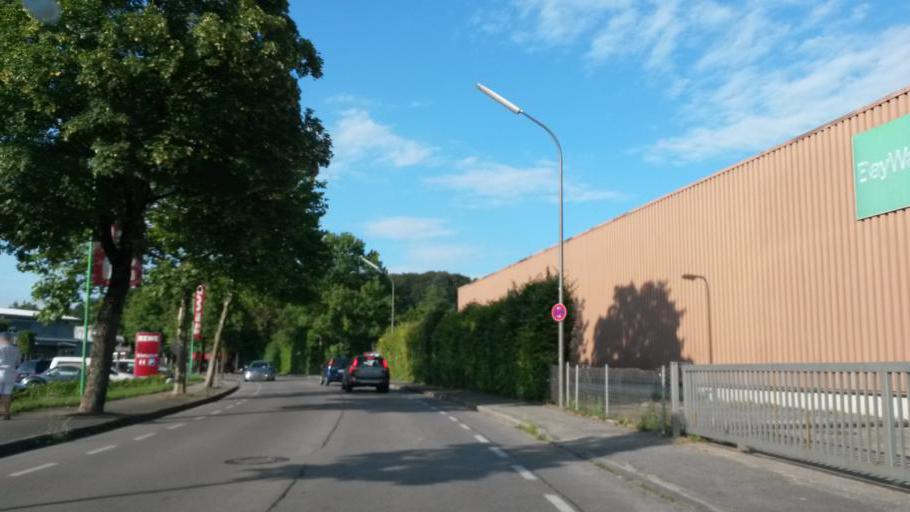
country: DE
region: Bavaria
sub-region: Upper Bavaria
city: Prien am Chiemsee
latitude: 47.8462
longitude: 12.3488
